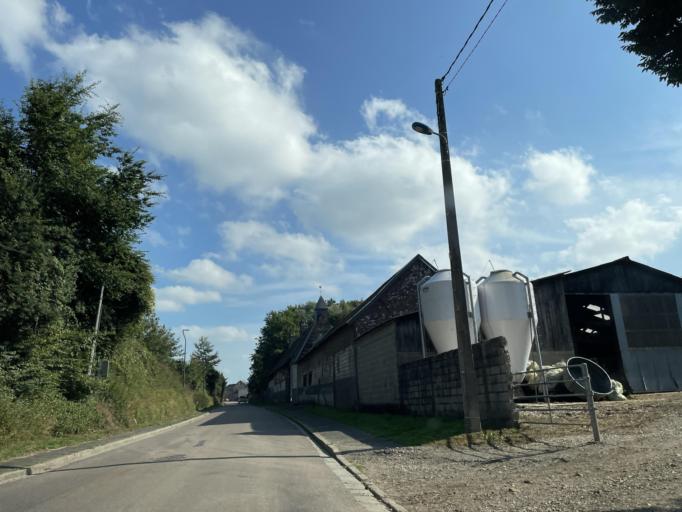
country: FR
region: Haute-Normandie
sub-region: Departement de la Seine-Maritime
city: Criel-sur-Mer
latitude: 50.0398
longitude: 1.3384
